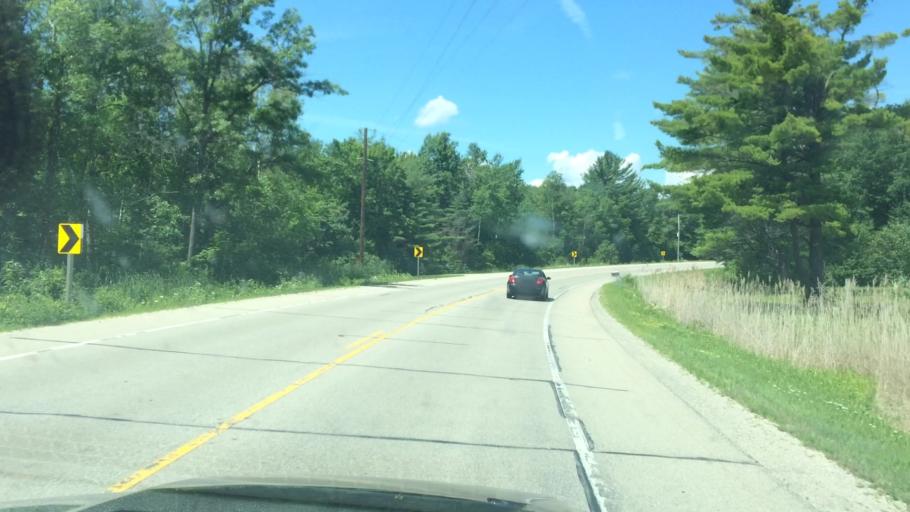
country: US
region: Wisconsin
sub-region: Marinette County
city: Peshtigo
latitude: 45.1005
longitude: -87.7423
